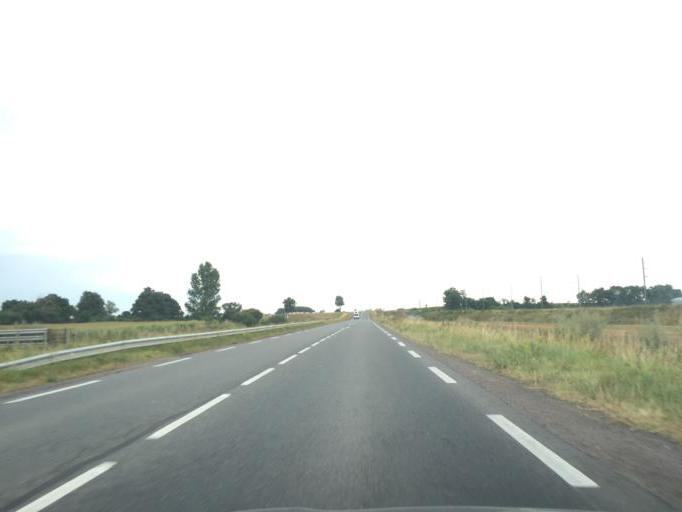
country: FR
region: Auvergne
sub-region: Departement de l'Allier
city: Bessay-sur-Allier
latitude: 46.4238
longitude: 3.3560
